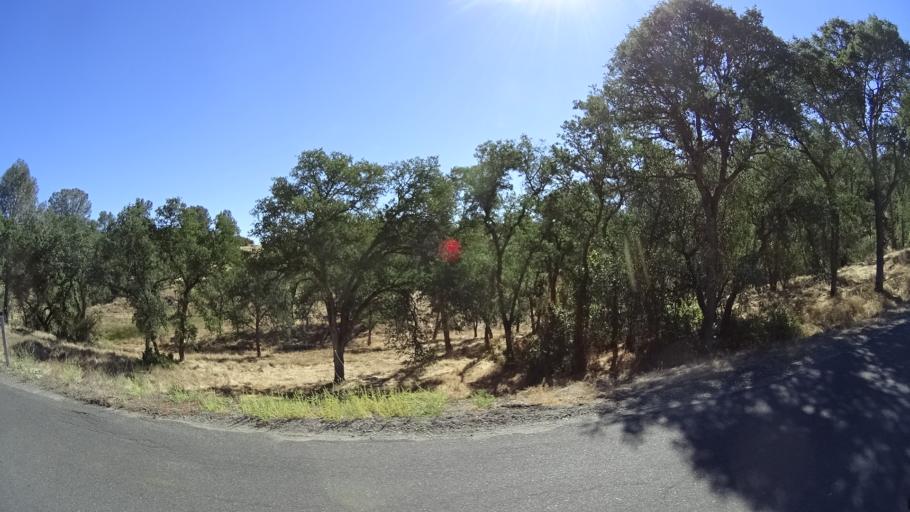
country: US
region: California
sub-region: Calaveras County
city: Rancho Calaveras
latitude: 38.1474
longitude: -120.8210
